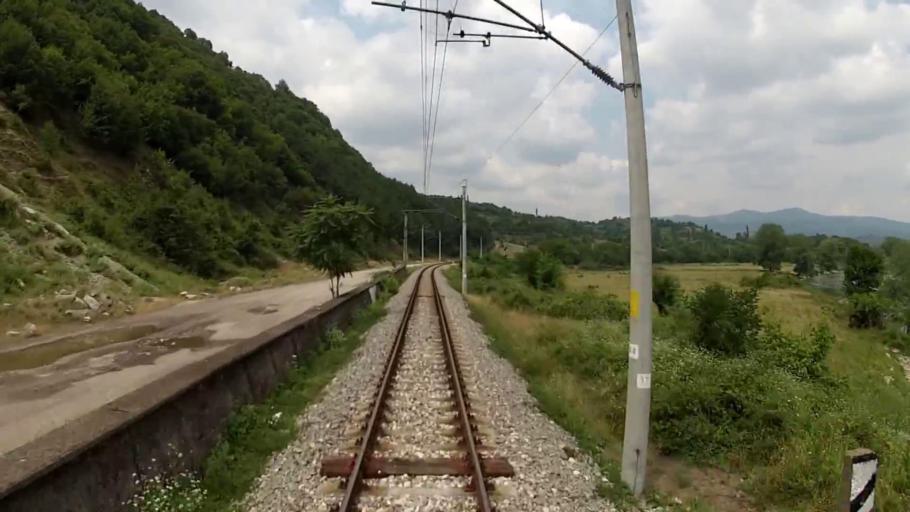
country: BG
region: Blagoevgrad
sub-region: Obshtina Simitli
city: Simitli
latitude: 41.8445
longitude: 23.1483
